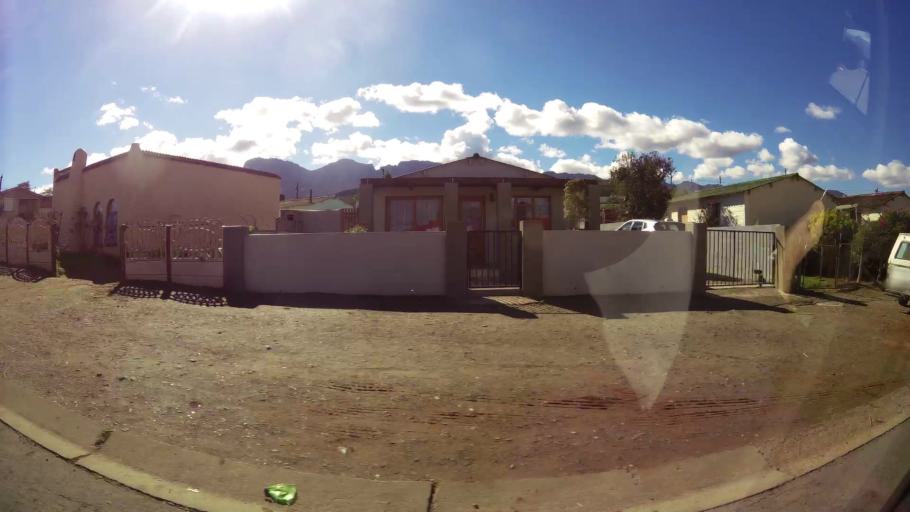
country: ZA
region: Western Cape
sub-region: Cape Winelands District Municipality
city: Ashton
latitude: -33.7911
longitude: 19.8975
